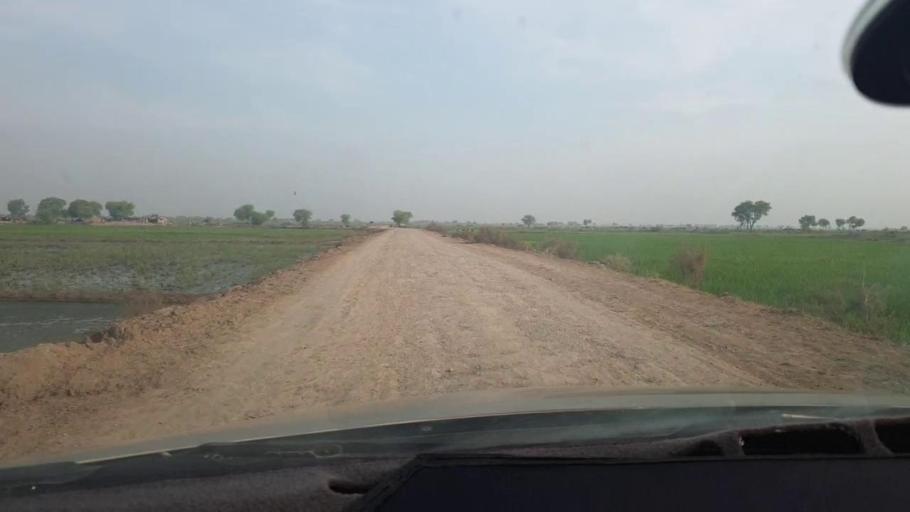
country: PK
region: Balochistan
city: Jhatpat
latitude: 28.3545
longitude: 68.4090
